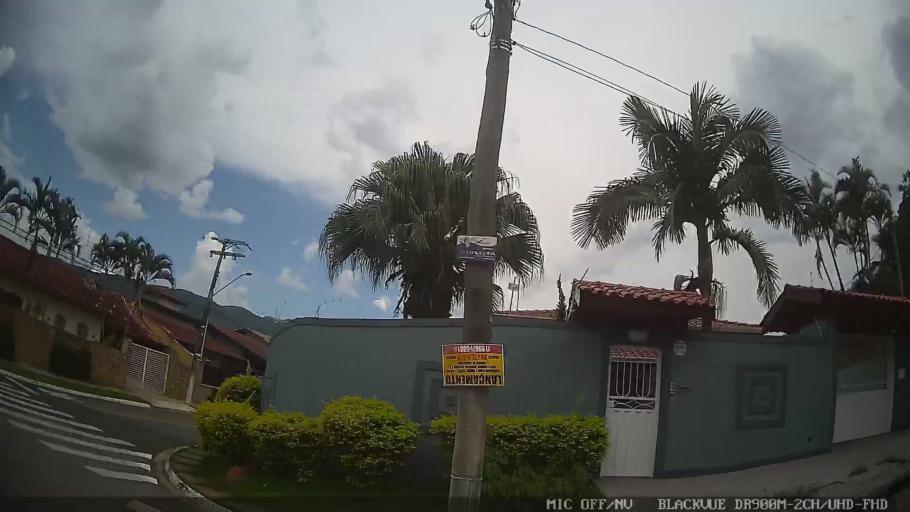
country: BR
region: Sao Paulo
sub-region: Atibaia
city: Atibaia
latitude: -23.1400
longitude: -46.5592
